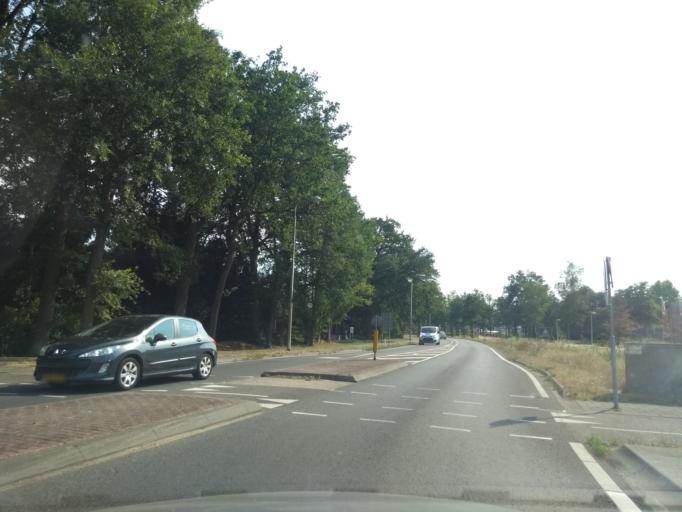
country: NL
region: Gelderland
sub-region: Gemeente Winterswijk
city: Winterswijk
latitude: 51.9804
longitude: 6.7049
